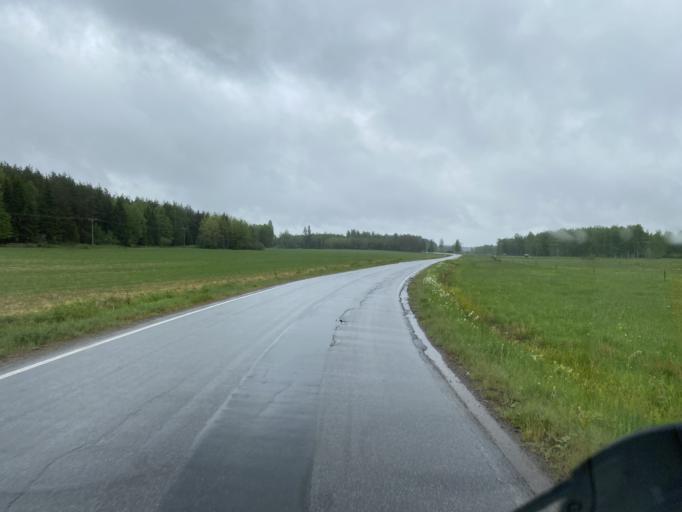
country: FI
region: Haeme
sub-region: Forssa
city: Humppila
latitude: 61.0414
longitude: 23.4028
